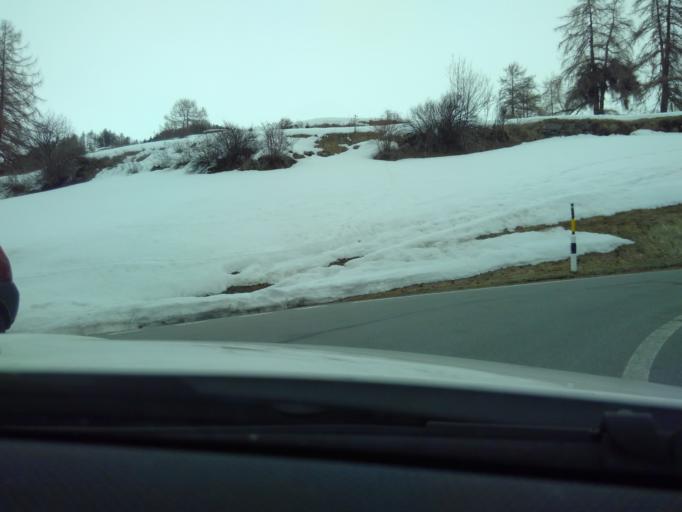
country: CH
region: Grisons
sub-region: Inn District
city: Zernez
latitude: 46.7757
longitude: 10.1439
